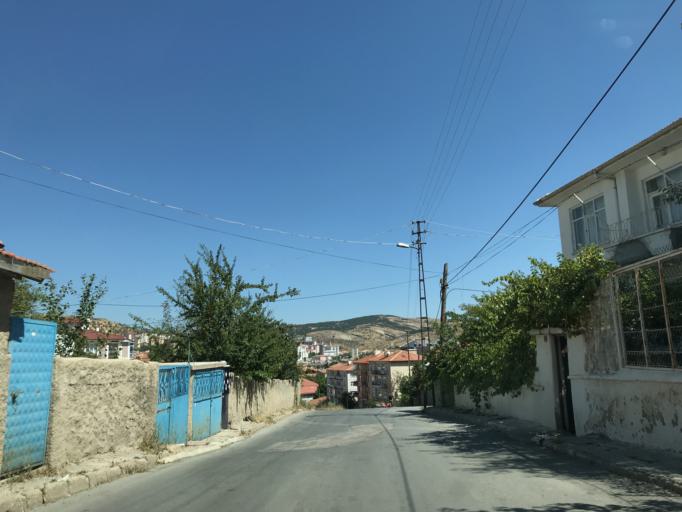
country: TR
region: Yozgat
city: Yozgat
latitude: 39.8189
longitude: 34.8174
